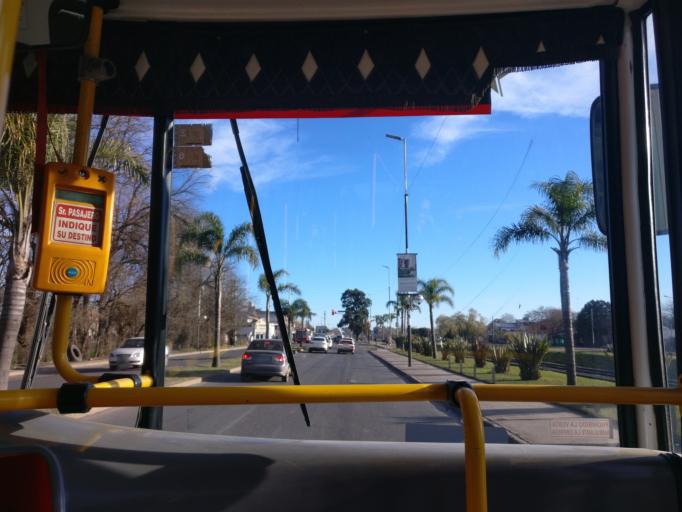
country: AR
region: Buenos Aires
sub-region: Partido de Ezeiza
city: Ezeiza
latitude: -34.8621
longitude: -58.5327
